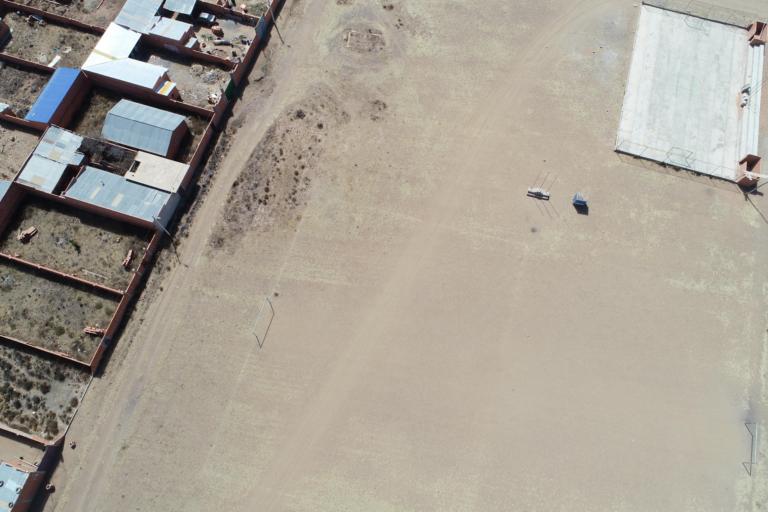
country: BO
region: La Paz
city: La Paz
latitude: -16.5939
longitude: -68.2123
